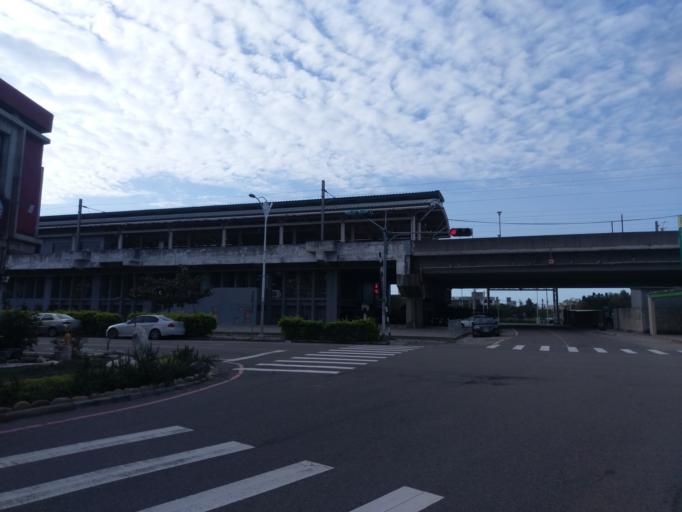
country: TW
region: Taiwan
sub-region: Miaoli
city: Miaoli
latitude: 24.6166
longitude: 120.7882
